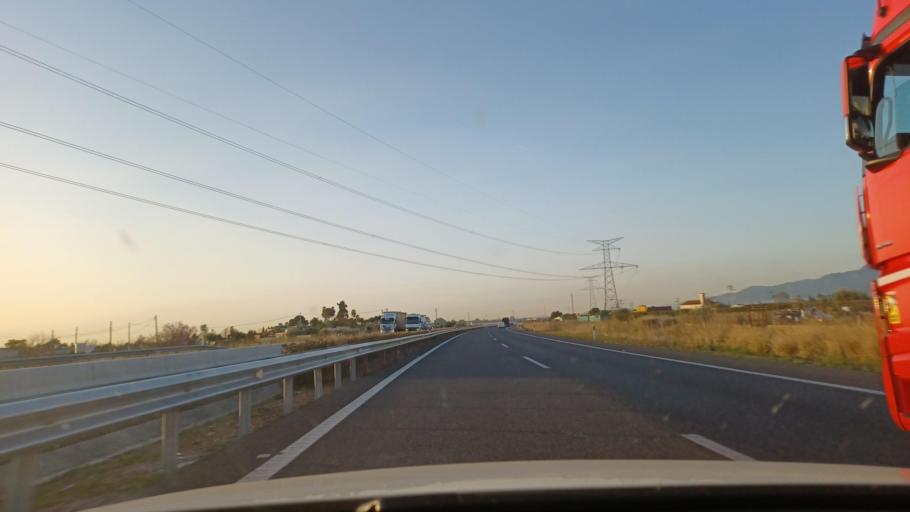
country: ES
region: Valencia
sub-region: Provincia de Castello
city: Vila-real
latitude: 39.9353
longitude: -0.1341
